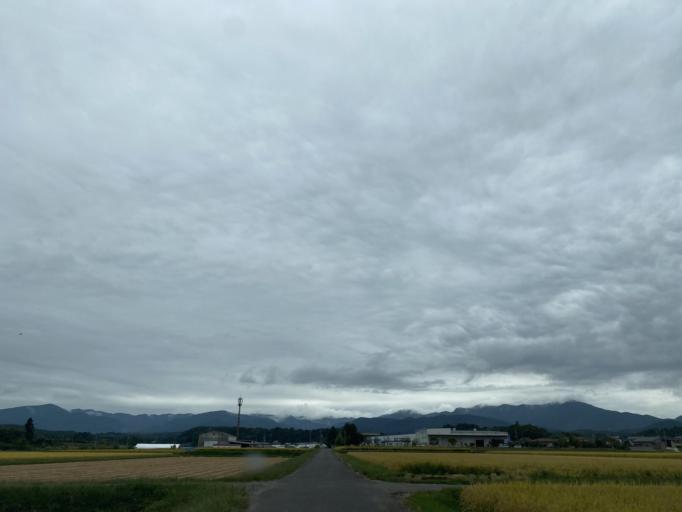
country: JP
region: Fukushima
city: Koriyama
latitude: 37.4179
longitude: 140.3120
